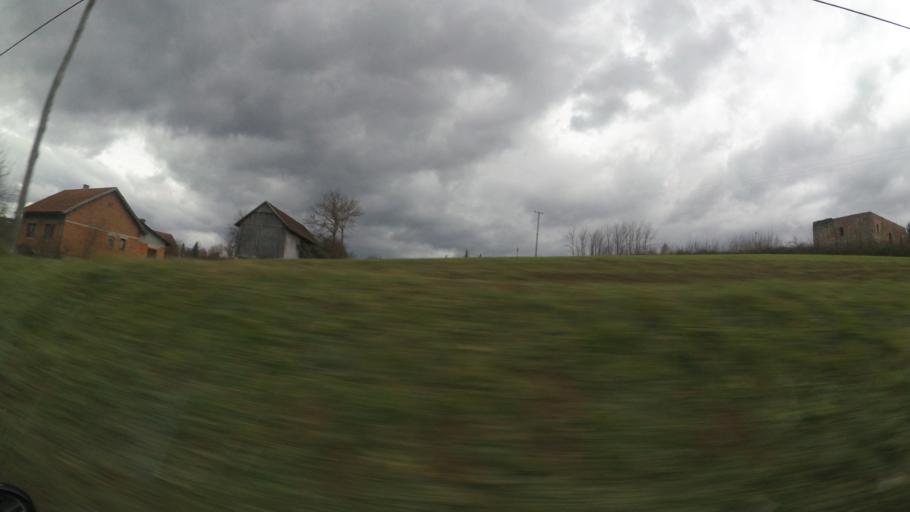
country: HR
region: Karlovacka
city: Vojnic
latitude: 45.3222
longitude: 15.6815
